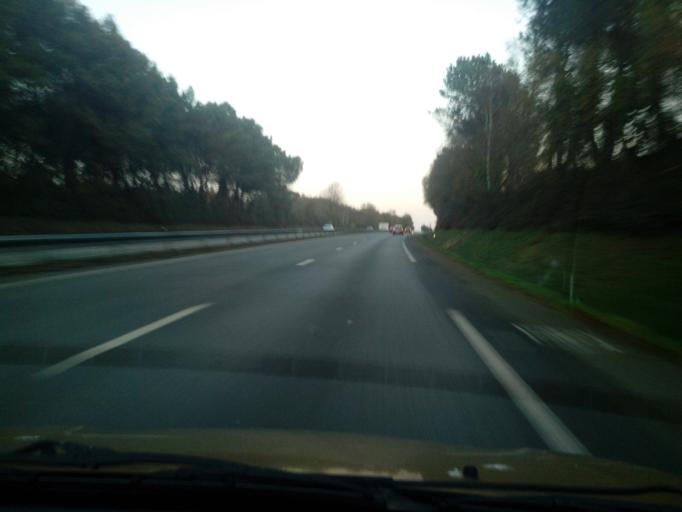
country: FR
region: Brittany
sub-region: Departement du Morbihan
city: Plumelin
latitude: 47.8945
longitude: -2.9187
